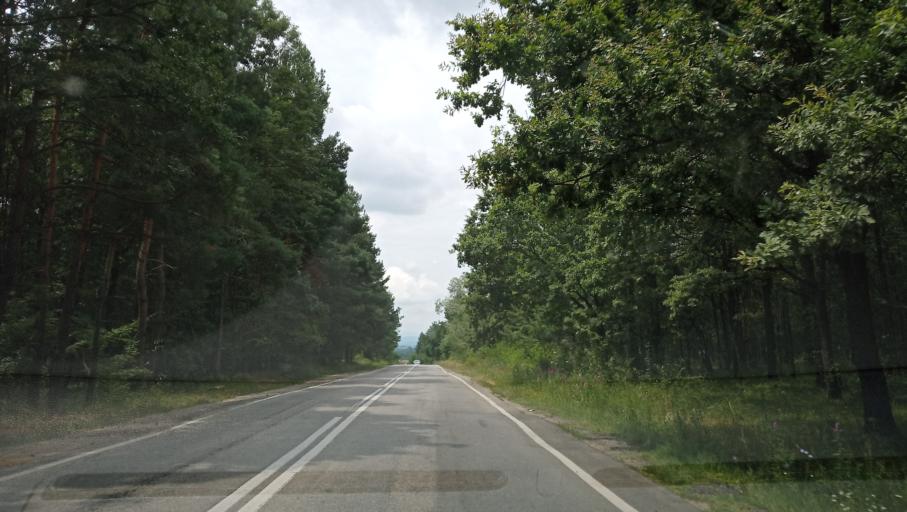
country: RO
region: Gorj
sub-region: Comuna Runcu
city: Balta
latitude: 45.0877
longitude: 23.1007
